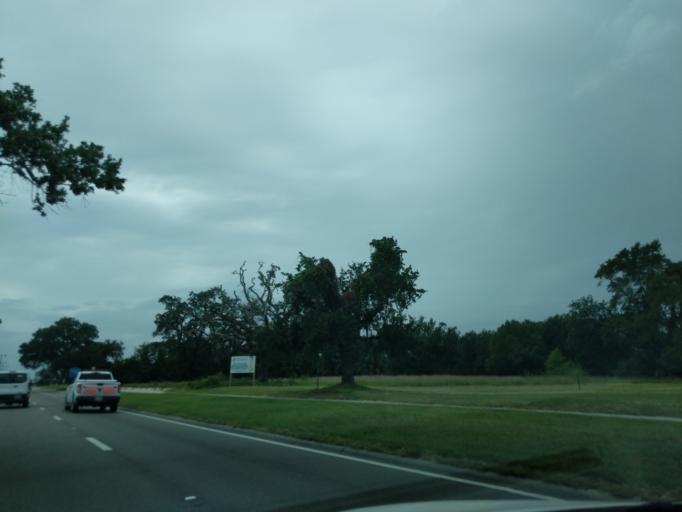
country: US
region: Mississippi
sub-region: Harrison County
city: Gulfport
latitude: 30.3615
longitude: -89.1050
